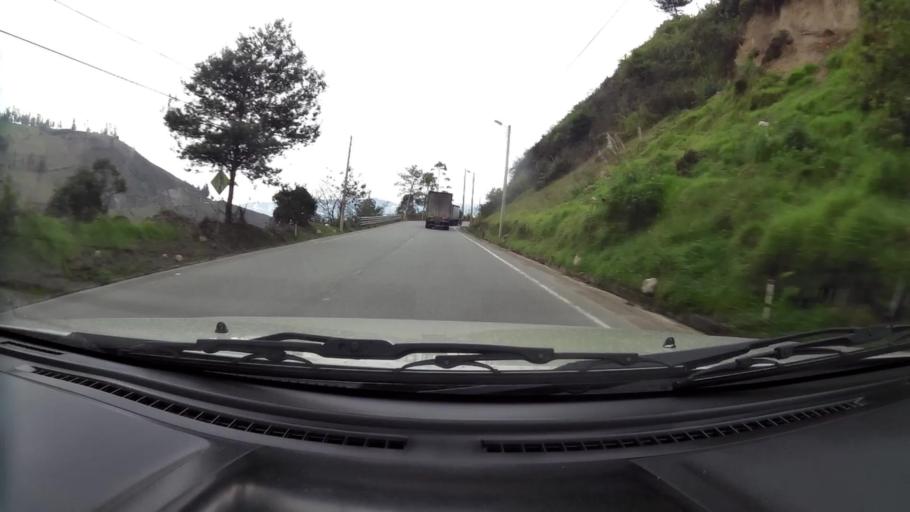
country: EC
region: Chimborazo
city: Alausi
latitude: -2.3053
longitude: -78.9083
